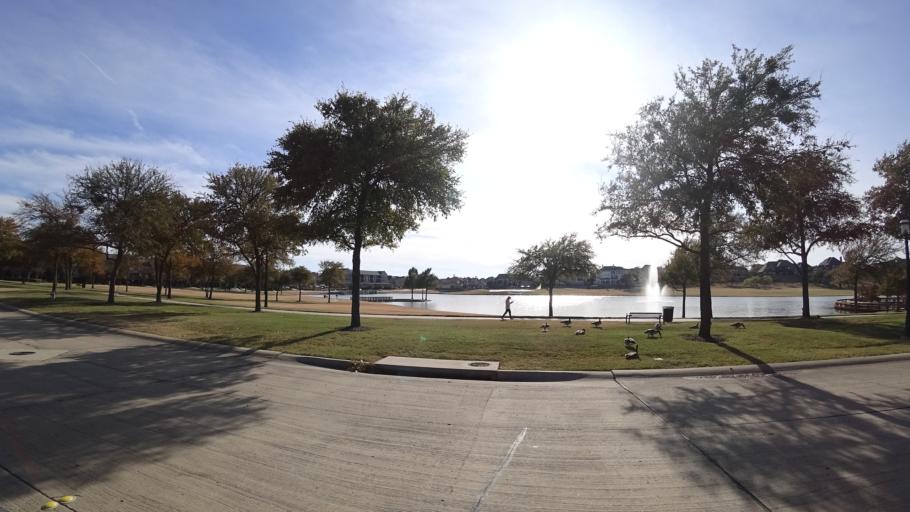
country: US
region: Texas
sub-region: Denton County
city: The Colony
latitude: 33.0375
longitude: -96.8987
